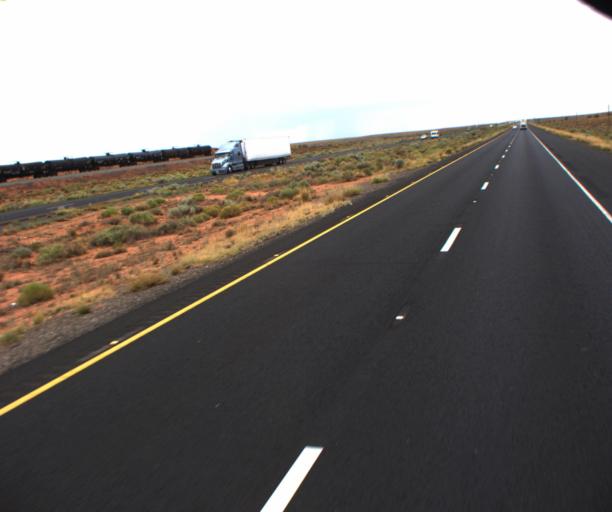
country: US
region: Arizona
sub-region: Coconino County
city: LeChee
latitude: 35.0586
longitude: -110.8047
